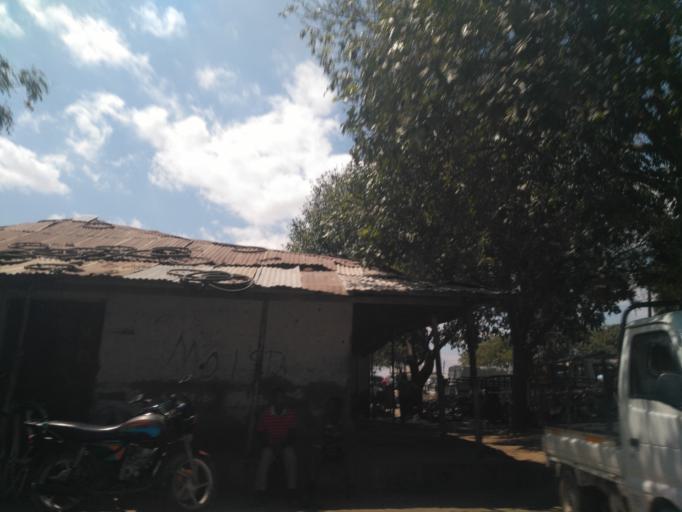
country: TZ
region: Dodoma
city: Dodoma
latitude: -6.1768
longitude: 35.7406
